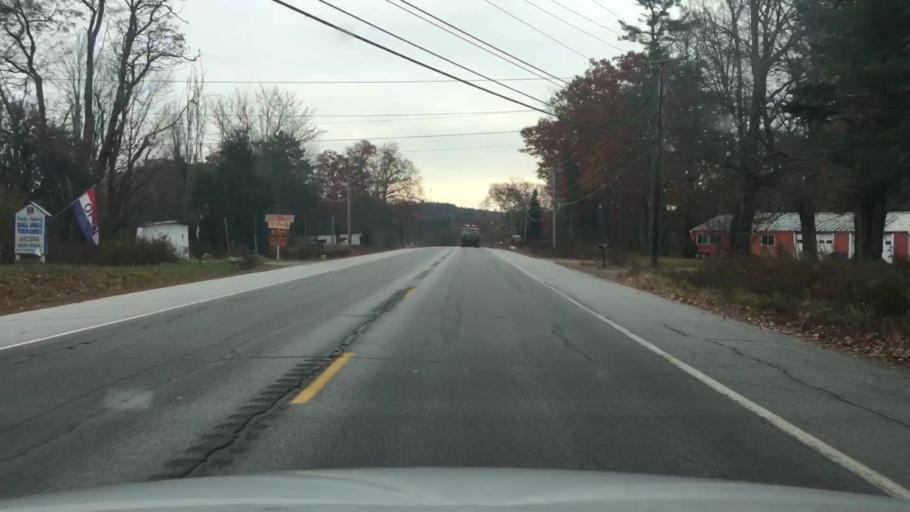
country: US
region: Maine
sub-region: Hancock County
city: Orland
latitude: 44.5646
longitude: -68.7159
